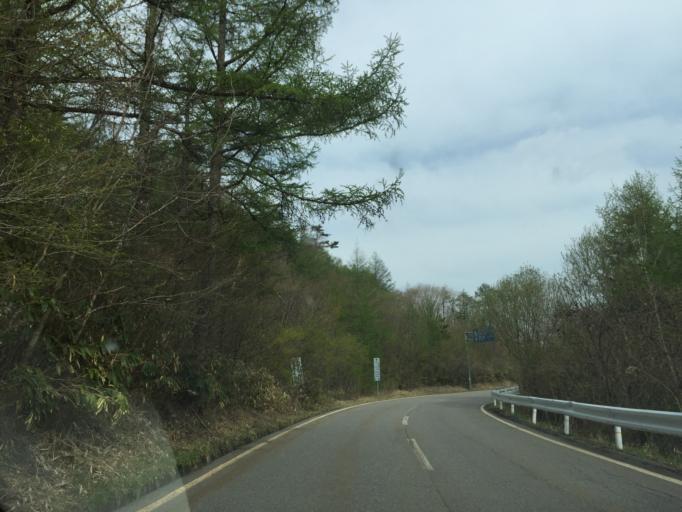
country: JP
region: Gifu
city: Nakatsugawa
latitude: 35.2977
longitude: 137.6692
